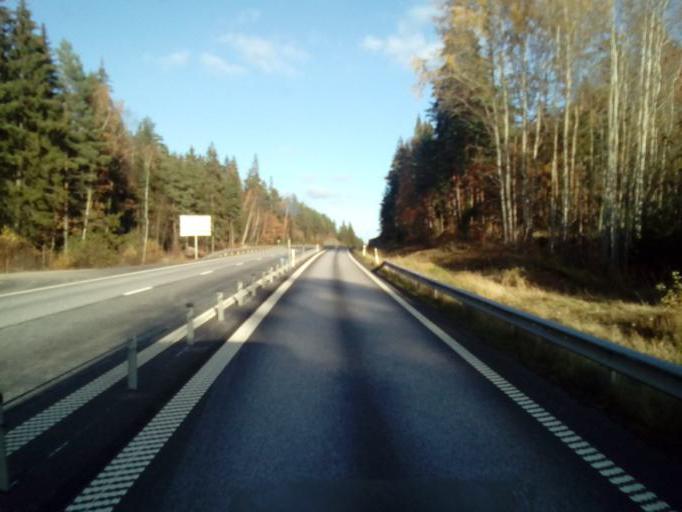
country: SE
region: Kalmar
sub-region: Vimmerby Kommun
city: Vimmerby
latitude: 57.7131
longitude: 16.0516
